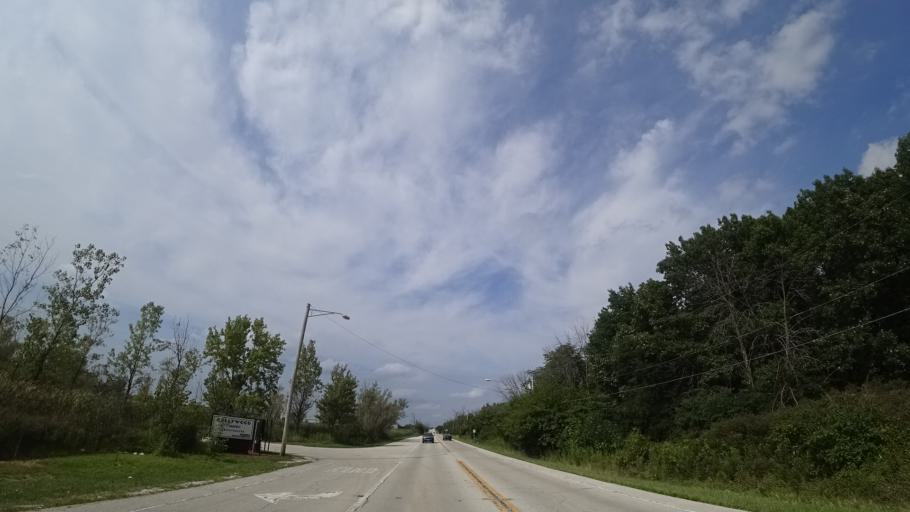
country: US
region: Illinois
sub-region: Cook County
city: Tinley Park
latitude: 41.5458
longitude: -87.7712
